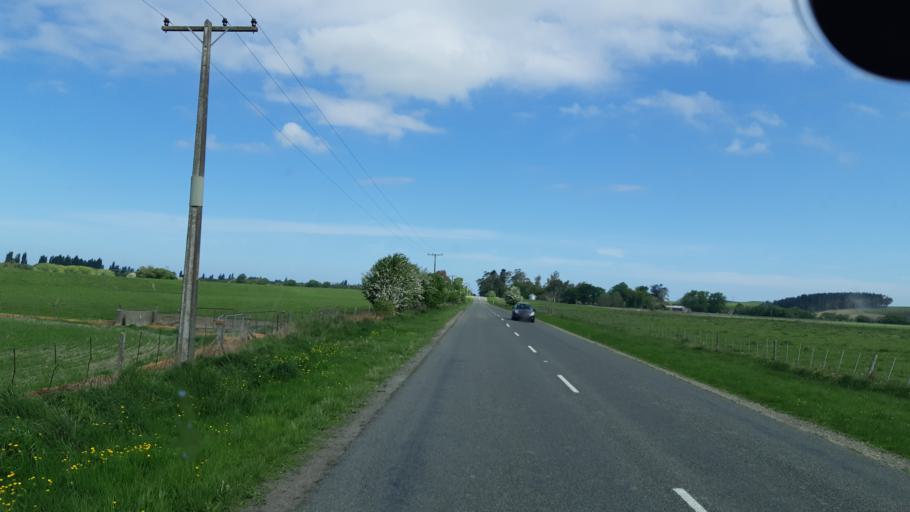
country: NZ
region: Canterbury
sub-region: Timaru District
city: Pleasant Point
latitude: -44.1750
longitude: 171.2212
